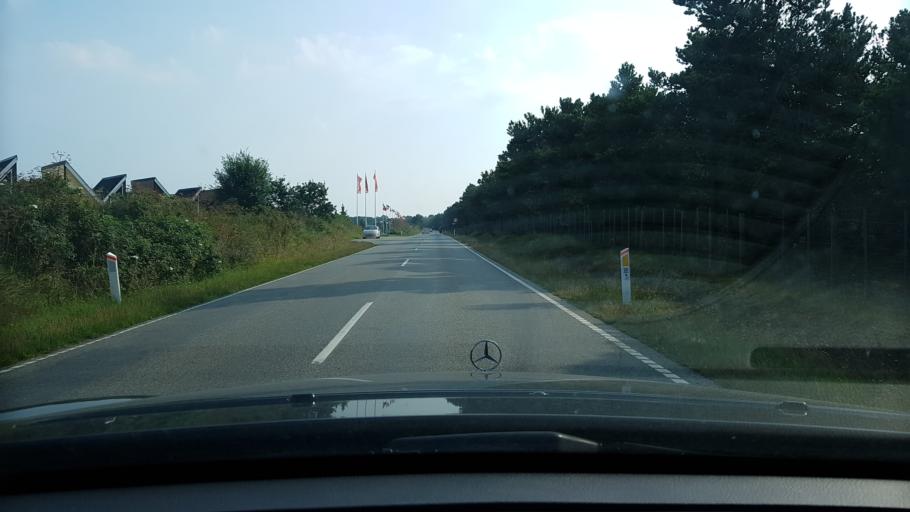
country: DK
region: North Denmark
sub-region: Alborg Kommune
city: Hals
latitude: 56.8269
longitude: 10.2687
